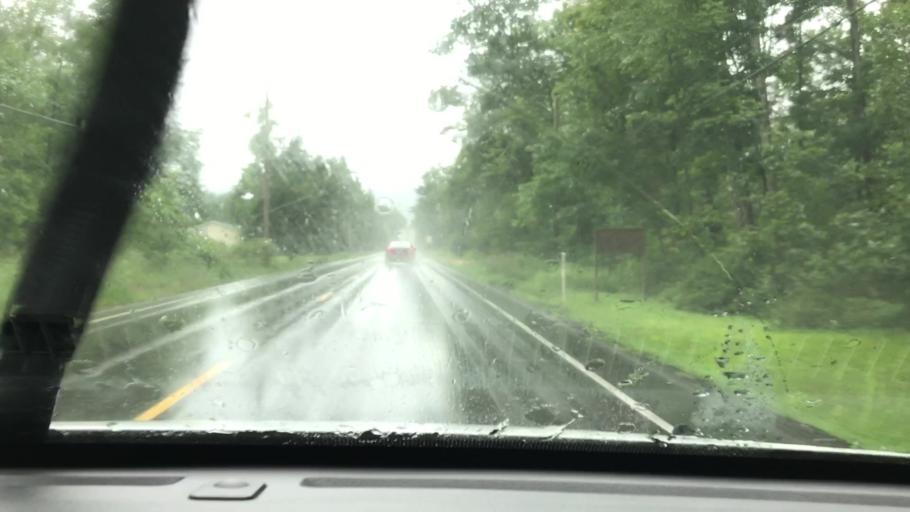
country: US
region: Pennsylvania
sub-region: Blair County
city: Tyrone
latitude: 40.7326
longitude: -78.1921
